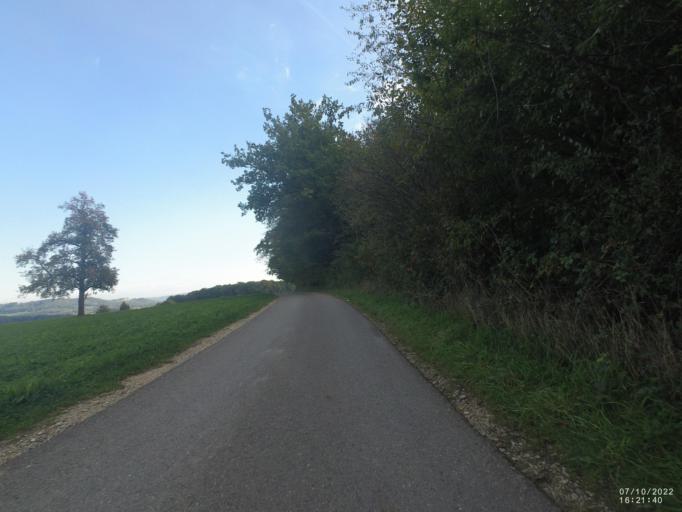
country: DE
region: Baden-Wuerttemberg
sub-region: Regierungsbezirk Stuttgart
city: Eislingen
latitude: 48.7131
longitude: 9.7236
